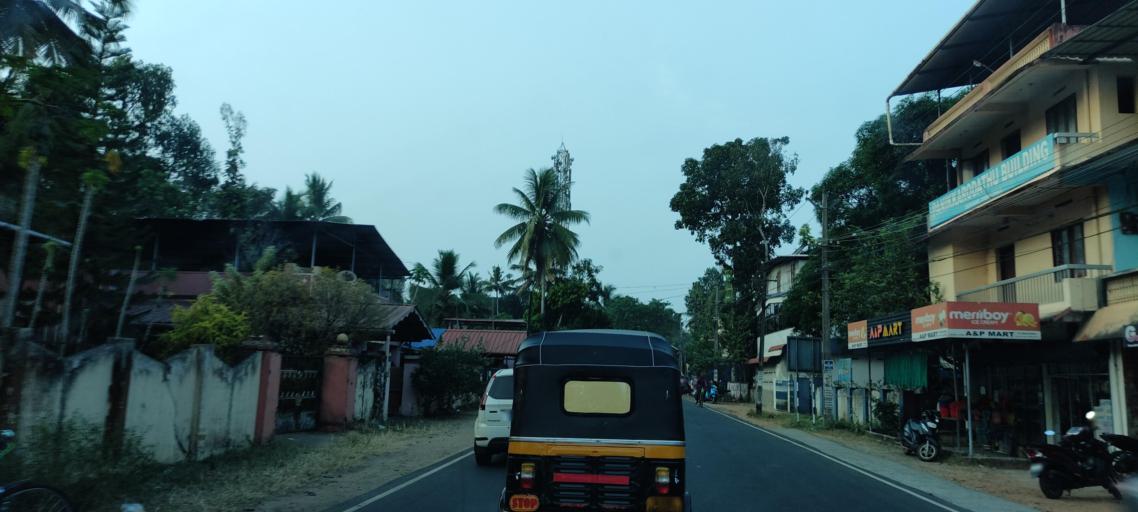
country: IN
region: Kerala
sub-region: Alappuzha
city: Mavelikara
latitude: 9.2903
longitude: 76.5325
